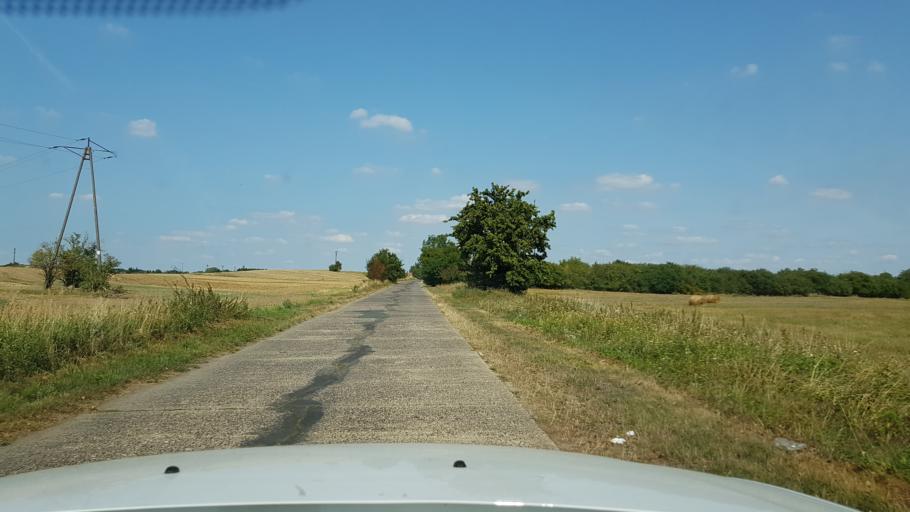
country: PL
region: West Pomeranian Voivodeship
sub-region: Powiat gryfinski
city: Moryn
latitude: 52.8429
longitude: 14.3859
